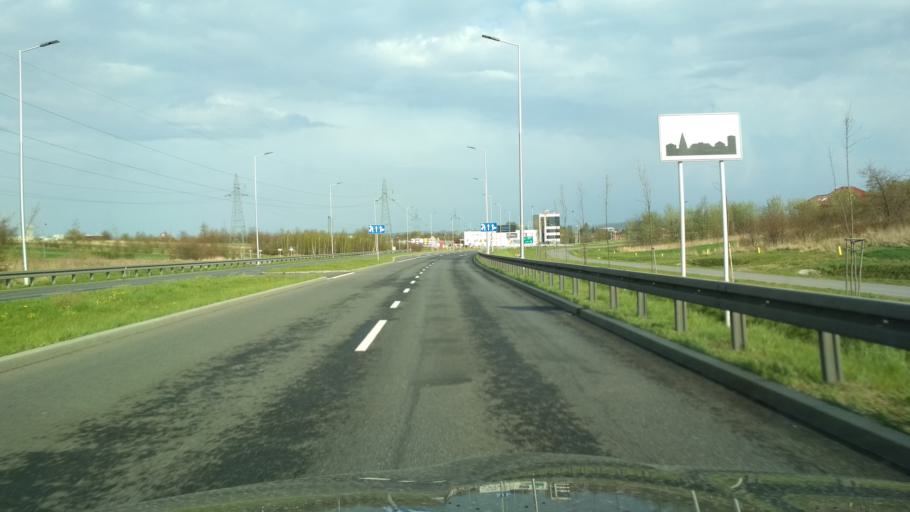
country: PL
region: Subcarpathian Voivodeship
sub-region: Powiat rzeszowski
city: Kielanowka
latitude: 50.0151
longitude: 21.9537
